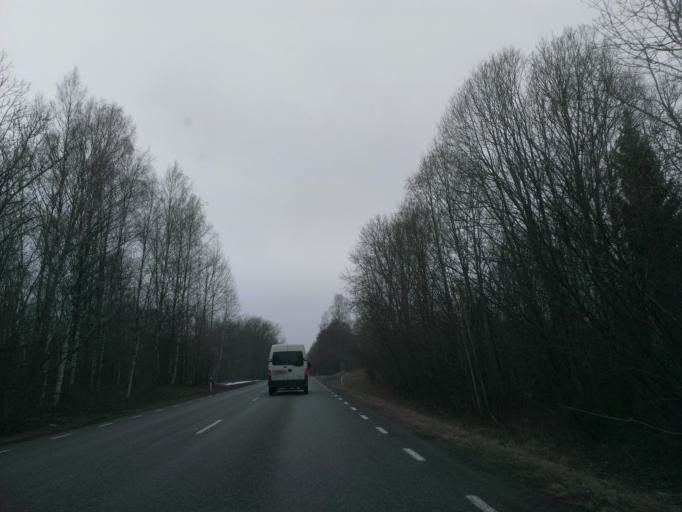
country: EE
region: Paernumaa
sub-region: Audru vald
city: Audru
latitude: 58.4880
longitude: 24.1464
